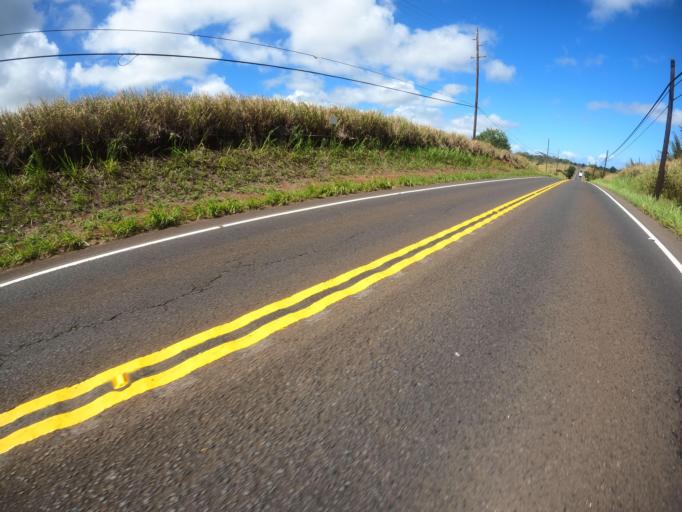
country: US
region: Hawaii
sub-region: Honolulu County
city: Waipi'o Acres
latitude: 21.4448
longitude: -158.0599
